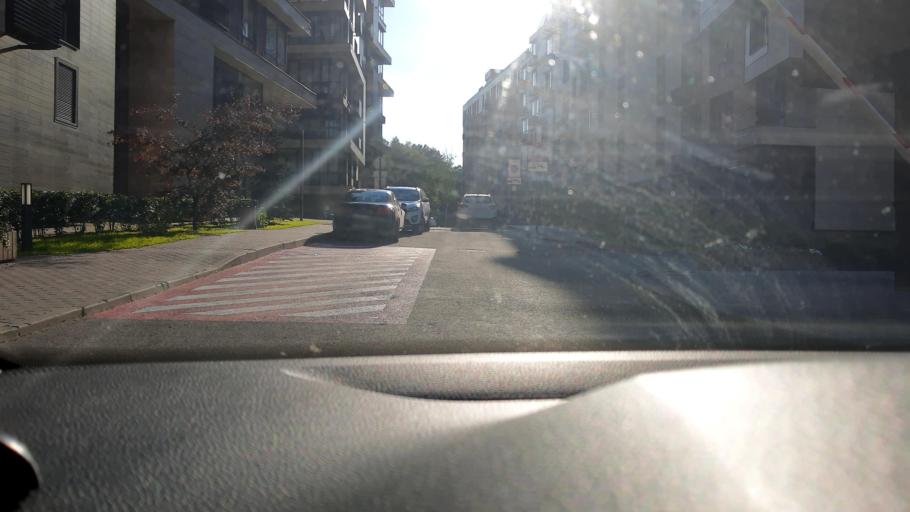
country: RU
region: Moskovskaya
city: Novopodrezkovo
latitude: 55.8946
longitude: 37.3731
